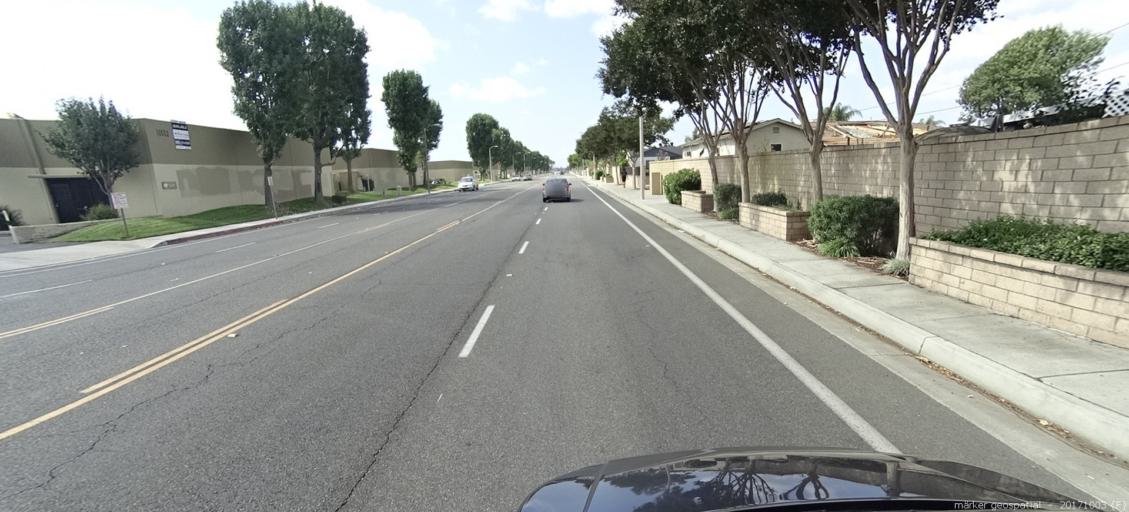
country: US
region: California
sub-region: Orange County
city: Garden Grove
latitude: 33.7669
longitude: -117.9447
